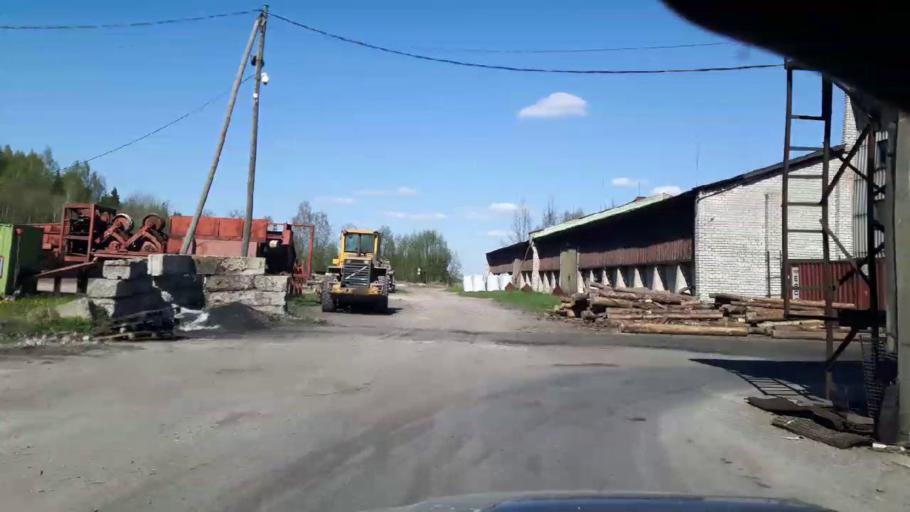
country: EE
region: Paernumaa
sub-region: Tootsi vald
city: Tootsi
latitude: 58.5227
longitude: 24.8193
